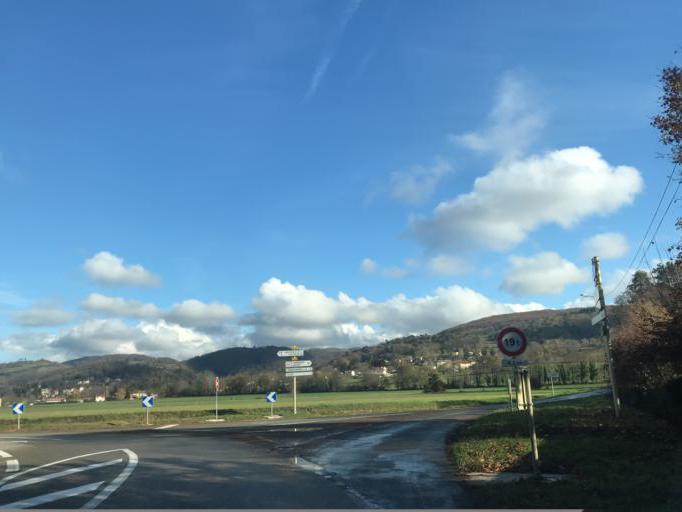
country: FR
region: Rhone-Alpes
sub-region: Departement de l'Ain
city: Saint-Jean-le-Vieux
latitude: 46.0294
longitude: 5.3926
